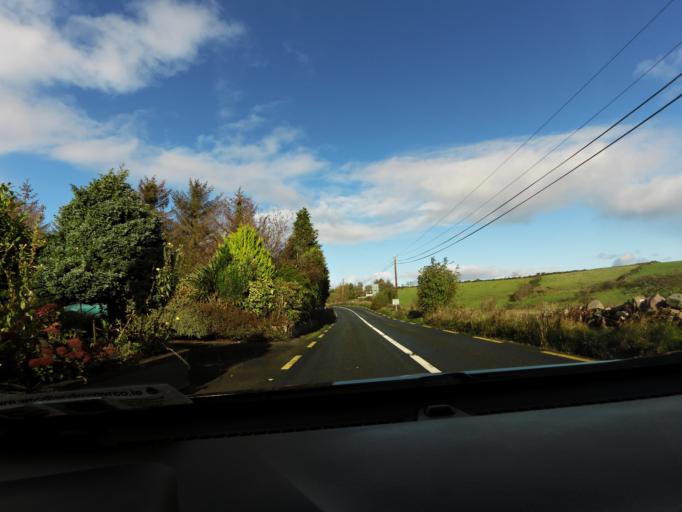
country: IE
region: Connaught
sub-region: Maigh Eo
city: Westport
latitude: 53.8199
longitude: -9.5337
